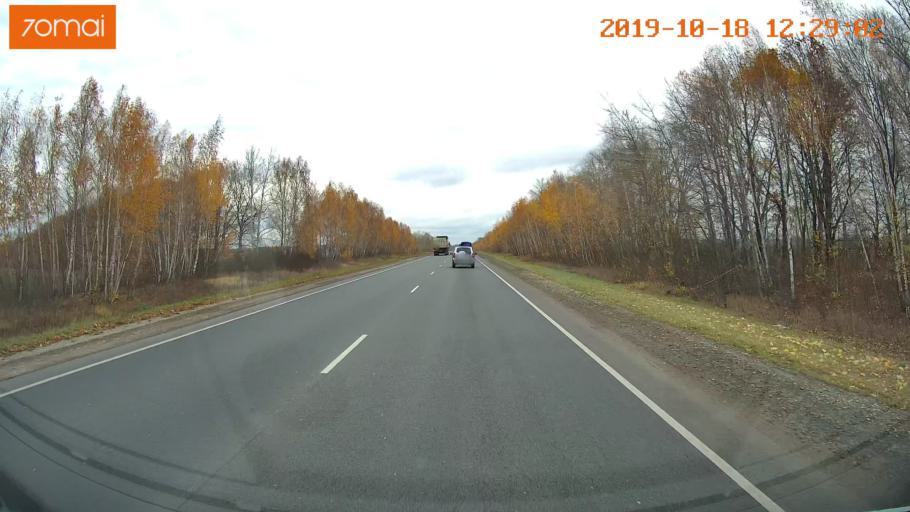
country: RU
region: Rjazan
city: Ryazan'
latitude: 54.5760
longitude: 39.5780
